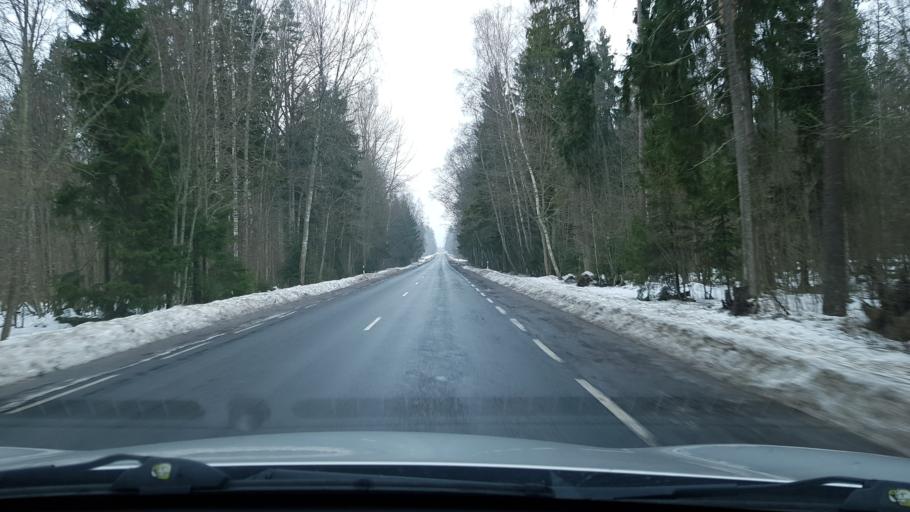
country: EE
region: Valgamaa
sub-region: Torva linn
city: Torva
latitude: 58.1725
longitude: 25.9626
